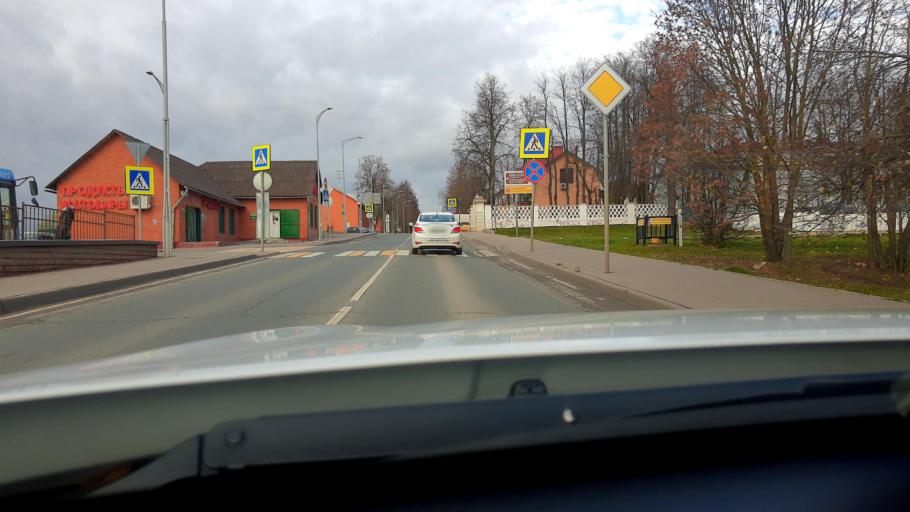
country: RU
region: Moskovskaya
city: Kokoshkino
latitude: 55.5353
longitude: 37.1523
